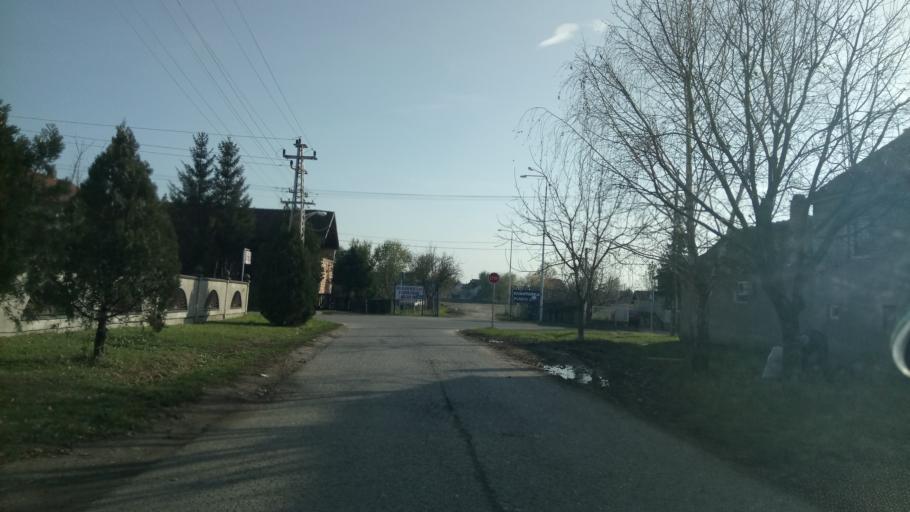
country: RS
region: Autonomna Pokrajina Vojvodina
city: Nova Pazova
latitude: 44.9525
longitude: 20.2214
